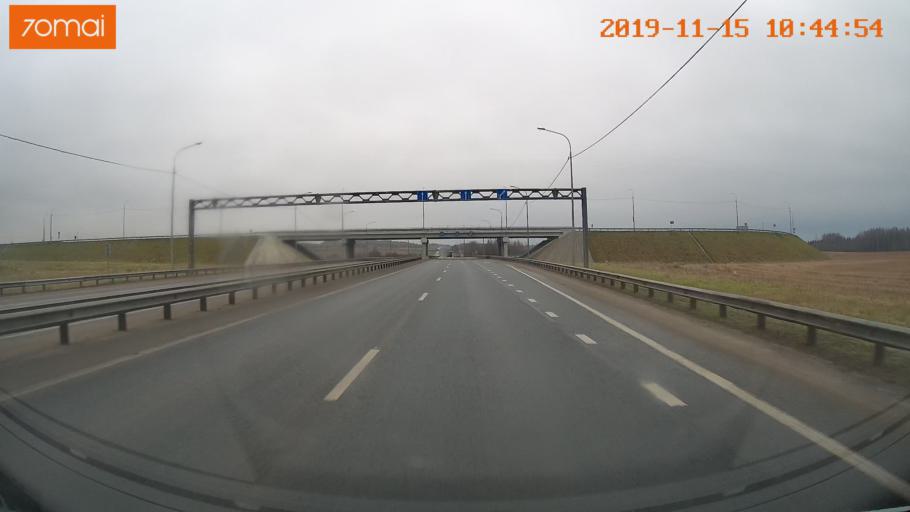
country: RU
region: Vologda
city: Sheksna
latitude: 59.2113
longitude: 38.5715
